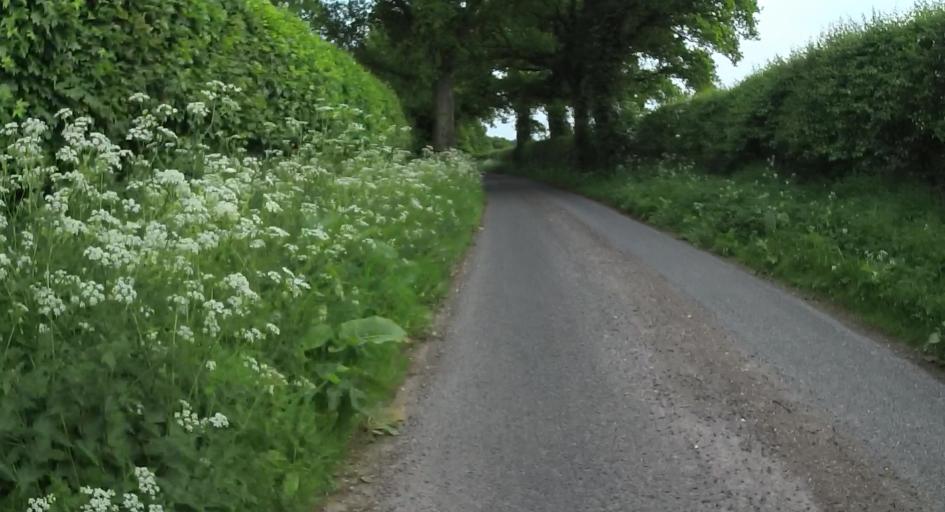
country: GB
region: England
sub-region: Hampshire
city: Overton
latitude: 51.2740
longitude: -1.2529
